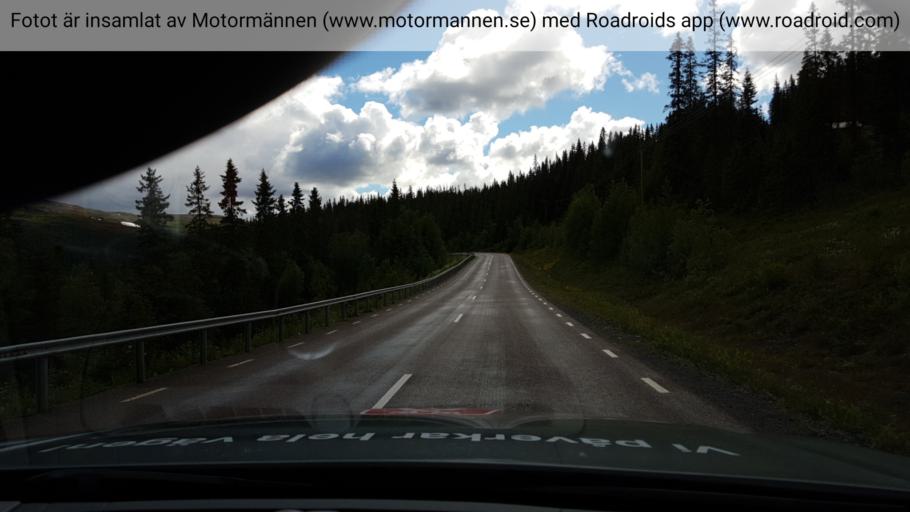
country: SE
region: Jaemtland
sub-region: Are Kommun
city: Jarpen
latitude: 63.0939
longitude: 13.7768
